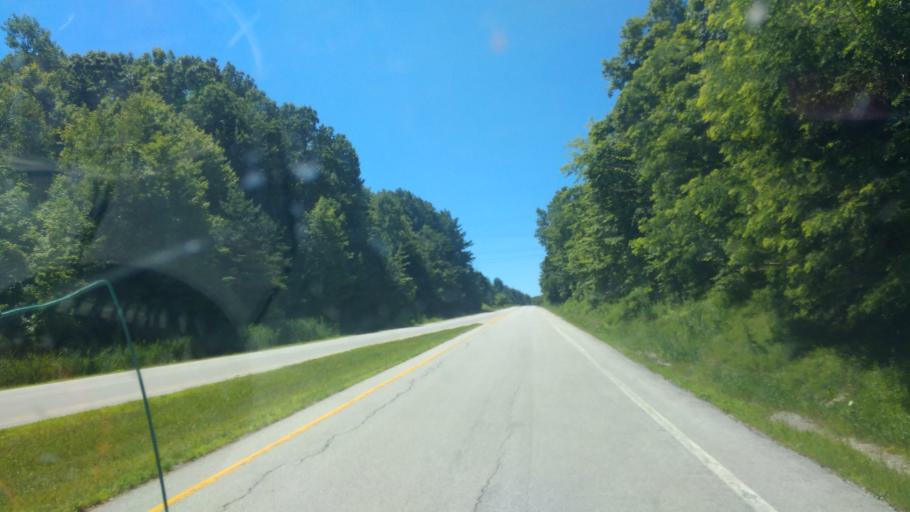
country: US
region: Ohio
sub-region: Ashtabula County
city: Conneaut
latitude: 41.9105
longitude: -80.5690
